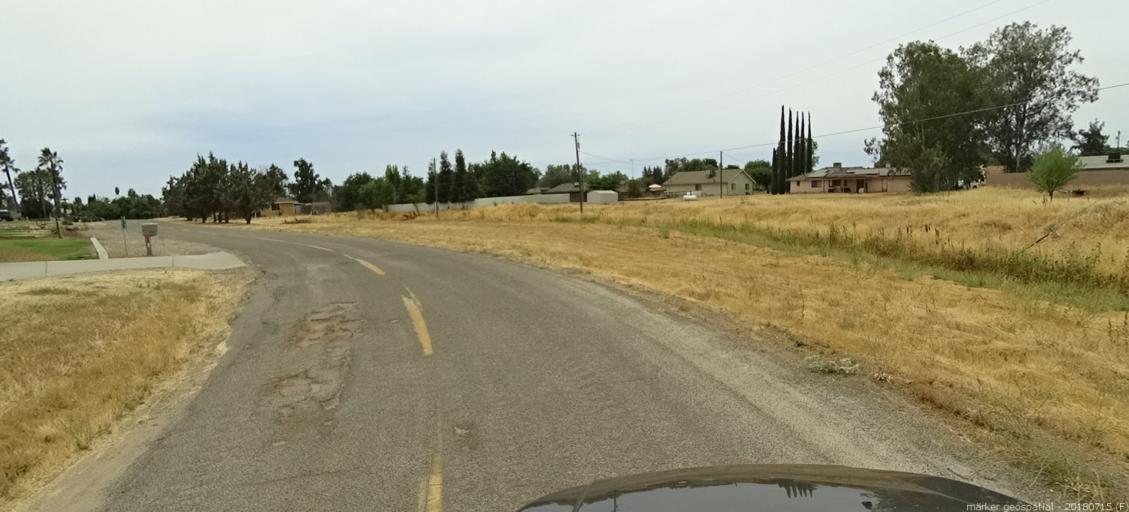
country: US
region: California
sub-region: Madera County
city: Madera Acres
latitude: 37.0139
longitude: -120.0785
